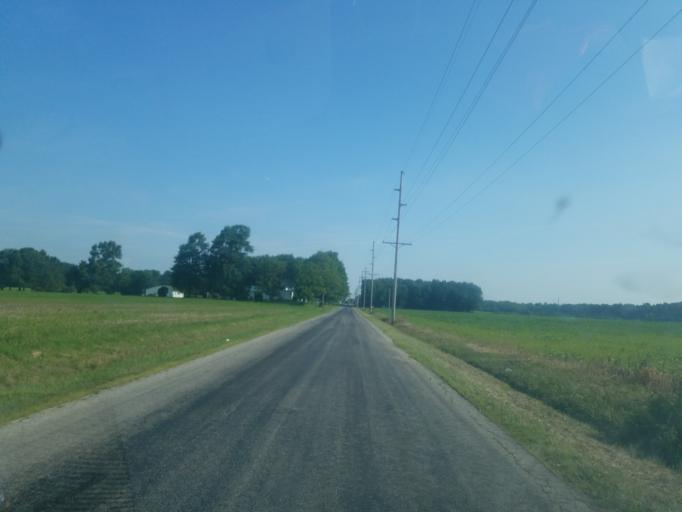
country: US
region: Ohio
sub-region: Richland County
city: Shelby
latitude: 40.9321
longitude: -82.6859
